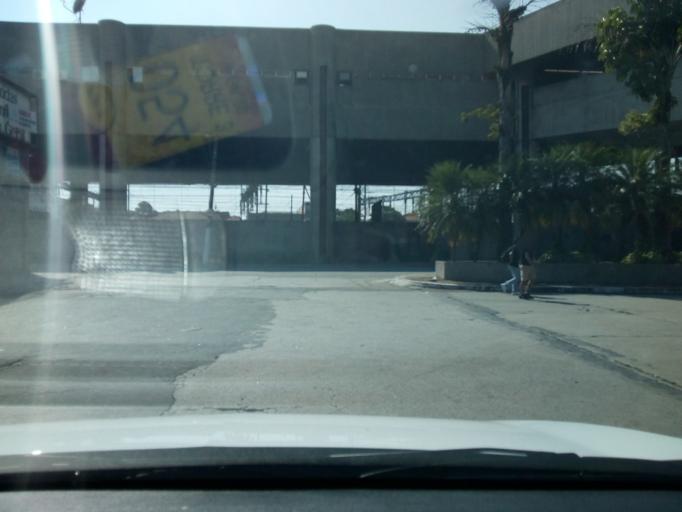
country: BR
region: Sao Paulo
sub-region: Sao Paulo
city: Sao Paulo
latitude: -23.5466
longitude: -46.6163
